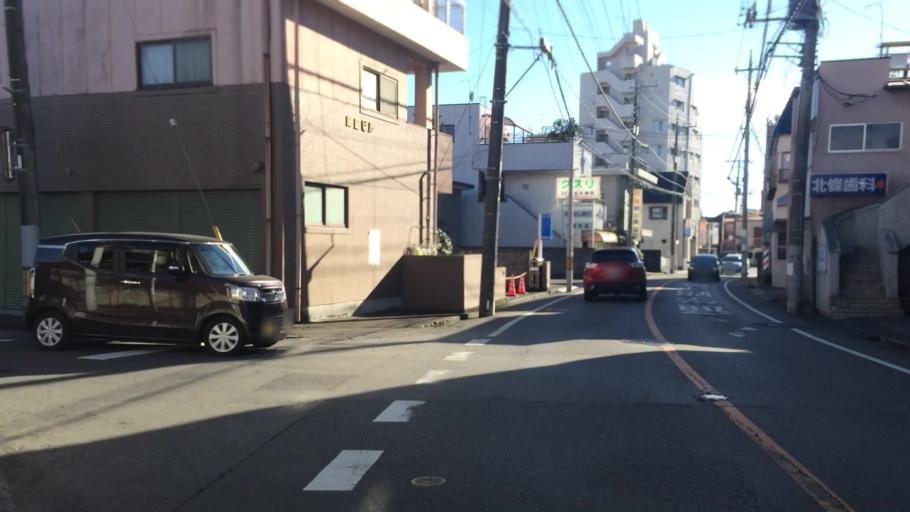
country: JP
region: Tochigi
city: Utsunomiya-shi
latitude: 36.5704
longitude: 139.8889
